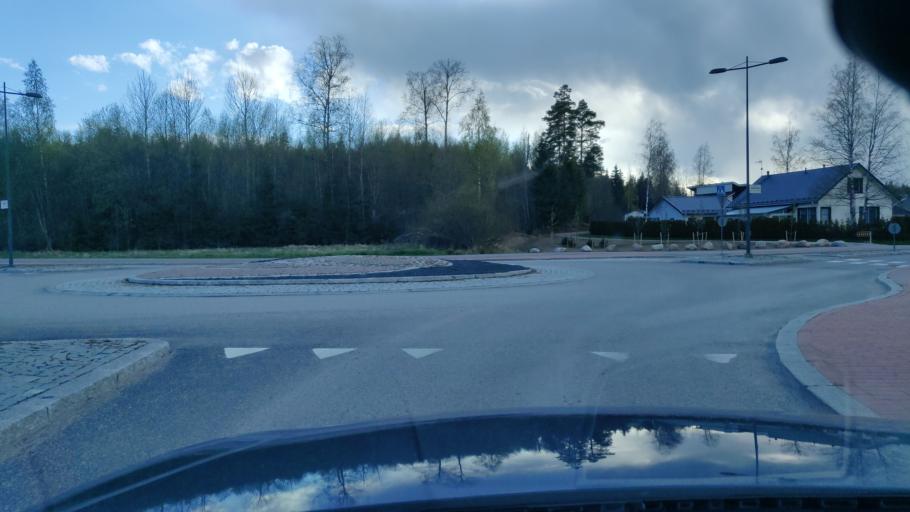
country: FI
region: Uusimaa
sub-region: Helsinki
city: Jaervenpaeae
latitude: 60.4855
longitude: 25.0579
